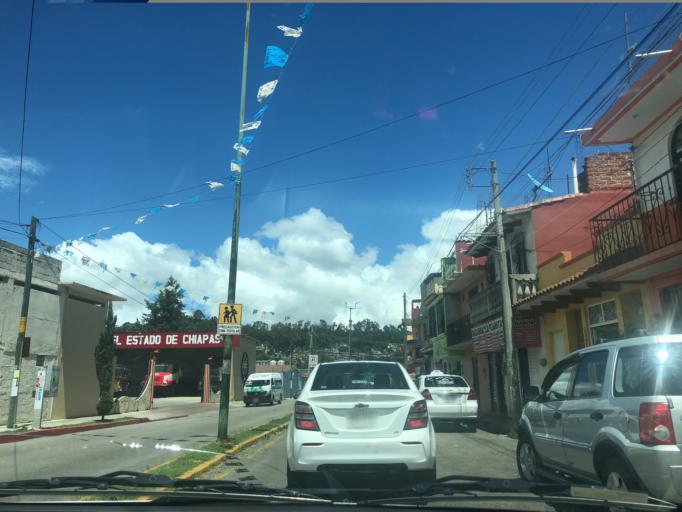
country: MX
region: Chiapas
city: San Cristobal de las Casas
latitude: 16.7256
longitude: -92.6407
